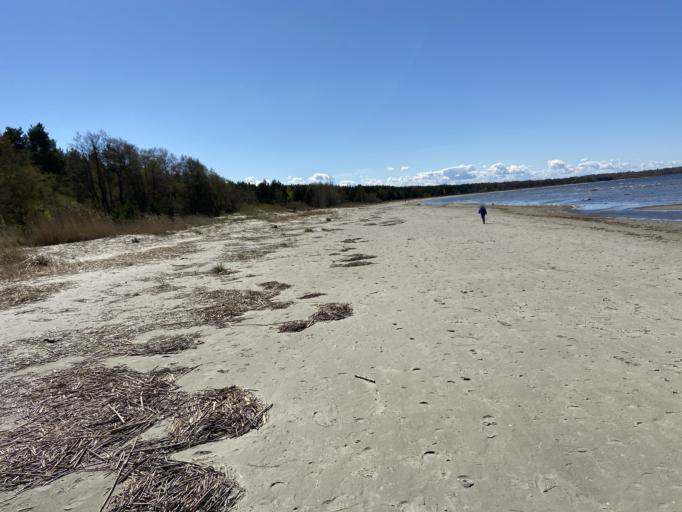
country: EE
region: Harju
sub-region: Raasiku vald
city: Raasiku
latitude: 59.4959
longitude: 25.1755
